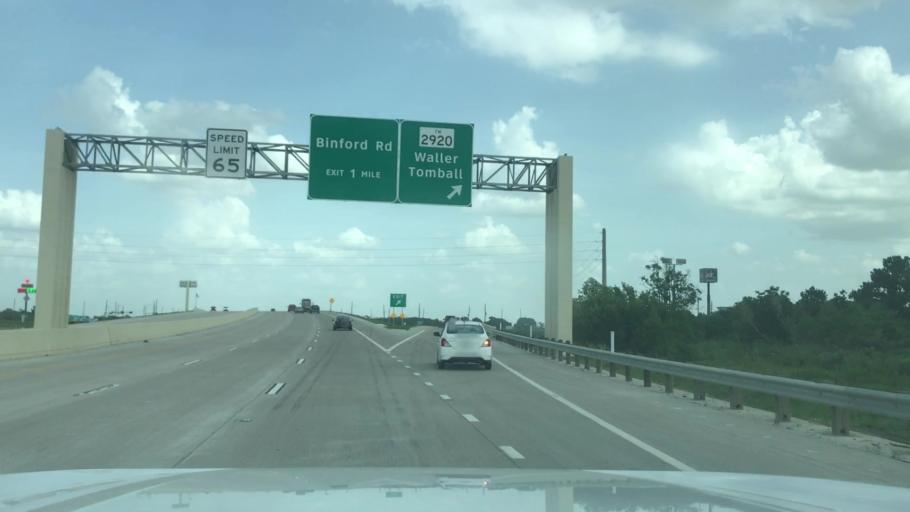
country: US
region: Texas
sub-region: Waller County
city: Waller
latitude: 30.0648
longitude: -95.9132
